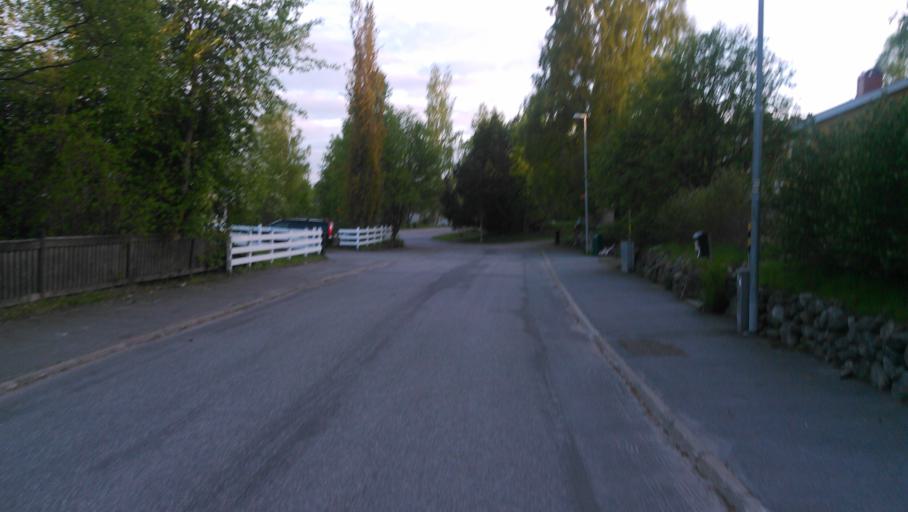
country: SE
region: Vaesterbotten
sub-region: Umea Kommun
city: Umea
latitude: 63.8303
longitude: 20.3078
